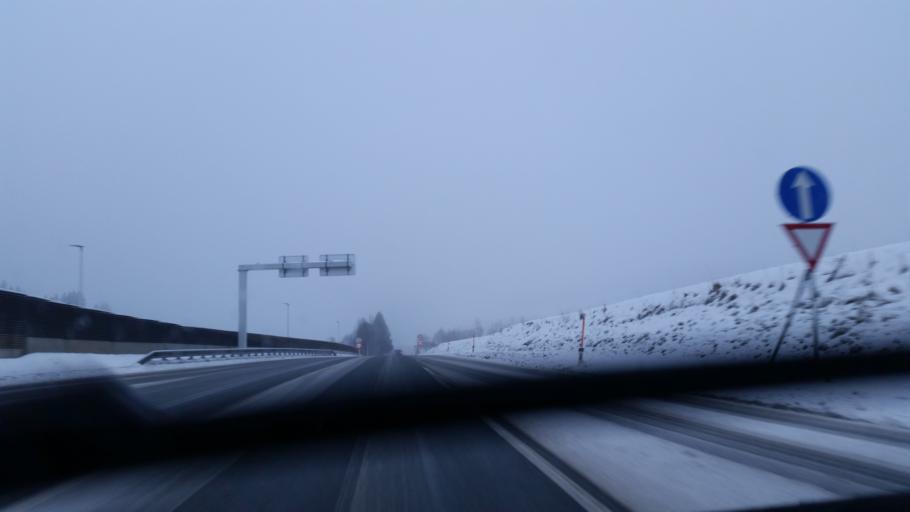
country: AT
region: Tyrol
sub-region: Politischer Bezirk Kufstein
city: Ellmau
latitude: 47.5168
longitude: 12.2955
